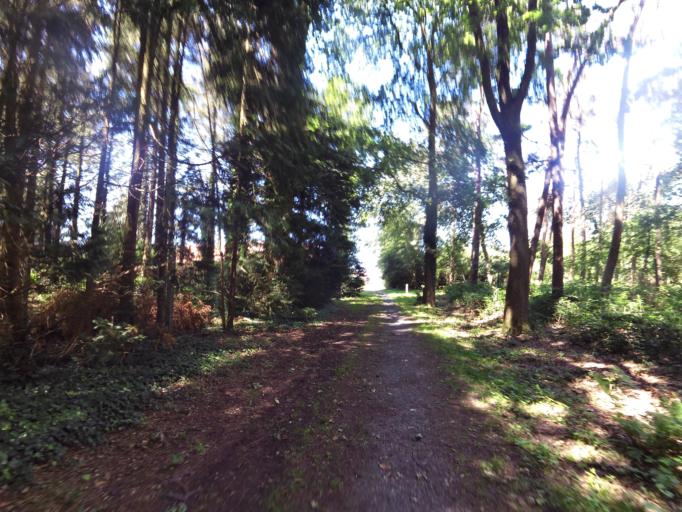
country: BE
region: Flanders
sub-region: Provincie West-Vlaanderen
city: Torhout
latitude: 51.0948
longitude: 3.0740
